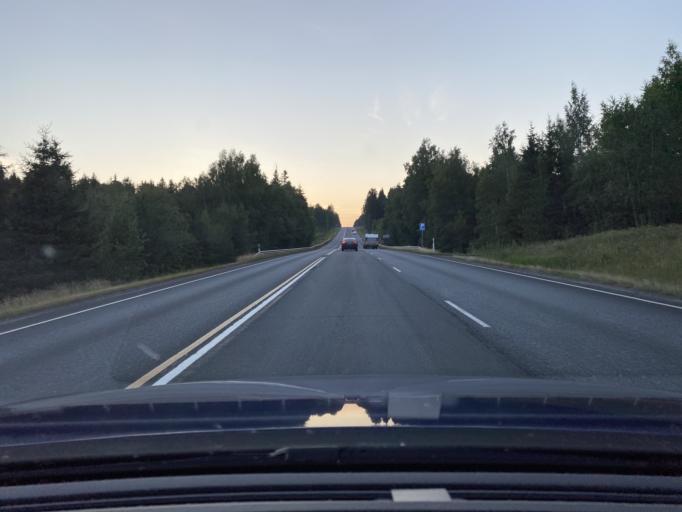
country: FI
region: Pirkanmaa
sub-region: Luoteis-Pirkanmaa
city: Ikaalinen
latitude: 61.7772
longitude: 23.0056
